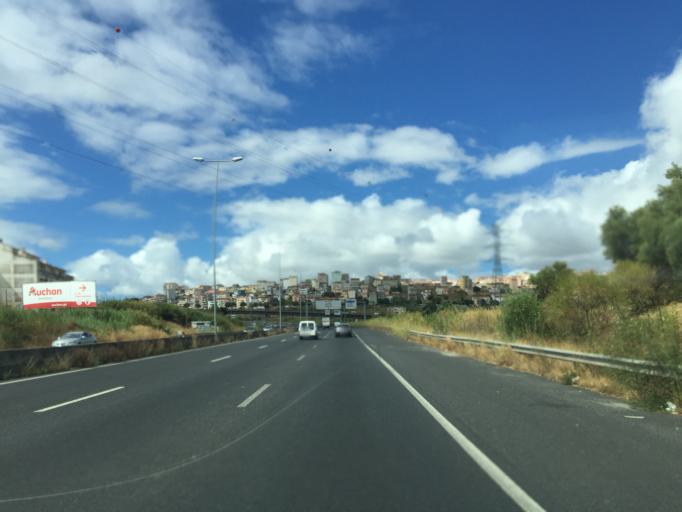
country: PT
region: Lisbon
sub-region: Odivelas
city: Pontinha
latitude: 38.7717
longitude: -9.2043
